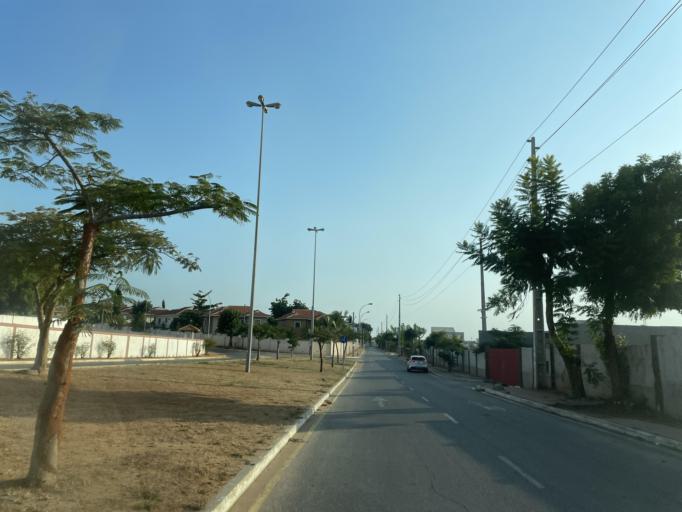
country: AO
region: Luanda
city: Luanda
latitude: -8.9250
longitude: 13.1792
